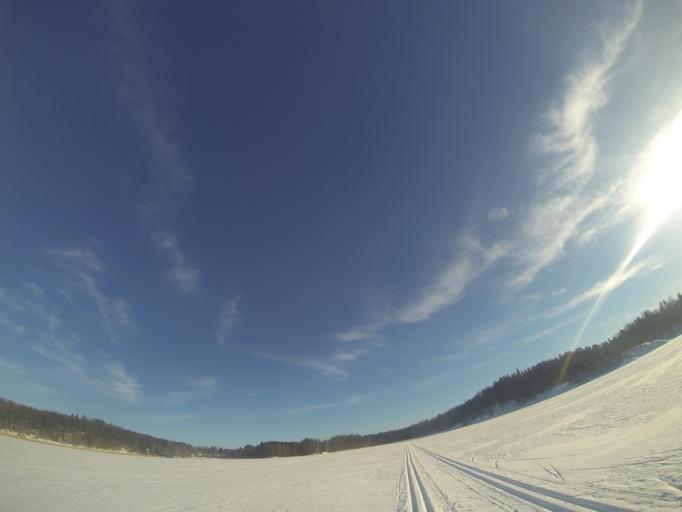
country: FI
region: Southern Savonia
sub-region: Savonlinna
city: Savonlinna
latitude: 61.8813
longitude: 28.9122
